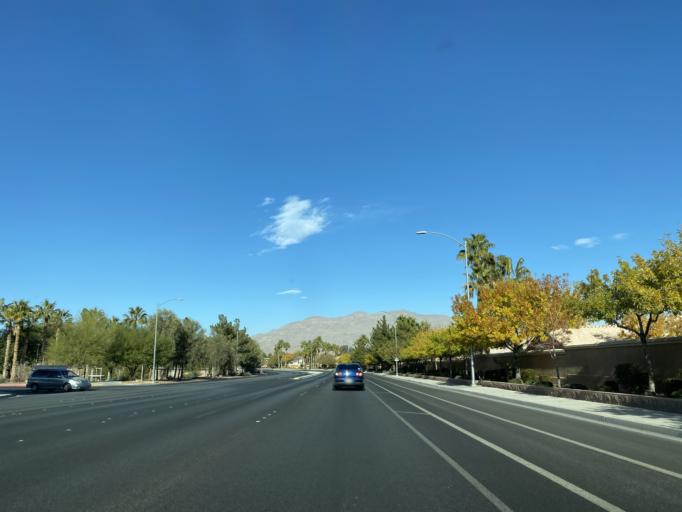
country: US
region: Nevada
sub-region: Clark County
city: Las Vegas
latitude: 36.2921
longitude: -115.2600
